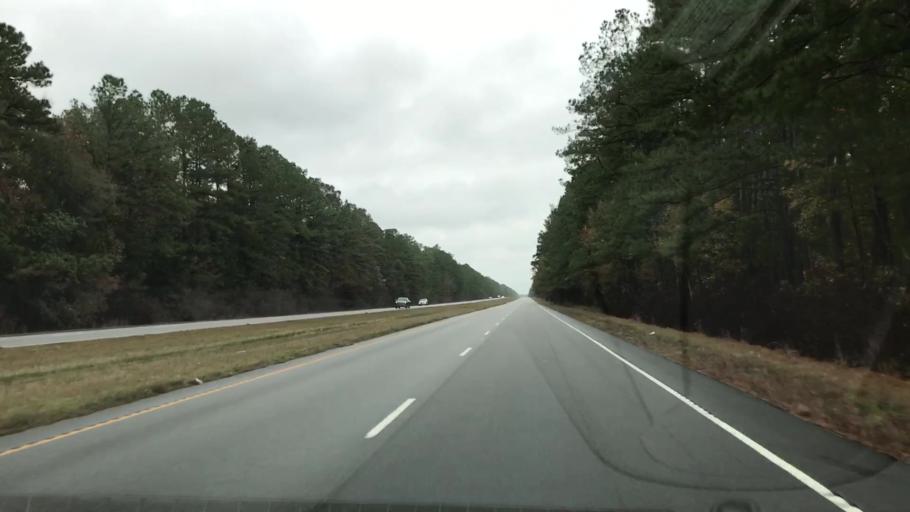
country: US
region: South Carolina
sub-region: Charleston County
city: Awendaw
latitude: 33.1461
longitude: -79.4360
